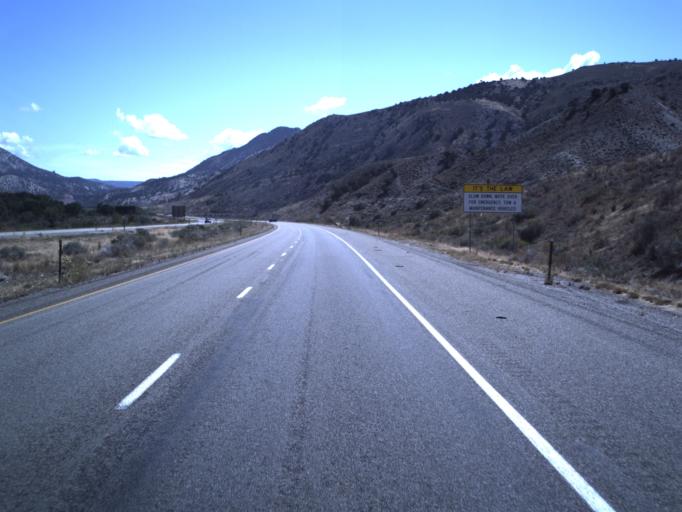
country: US
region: Utah
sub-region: Sevier County
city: Salina
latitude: 38.9312
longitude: -111.8411
